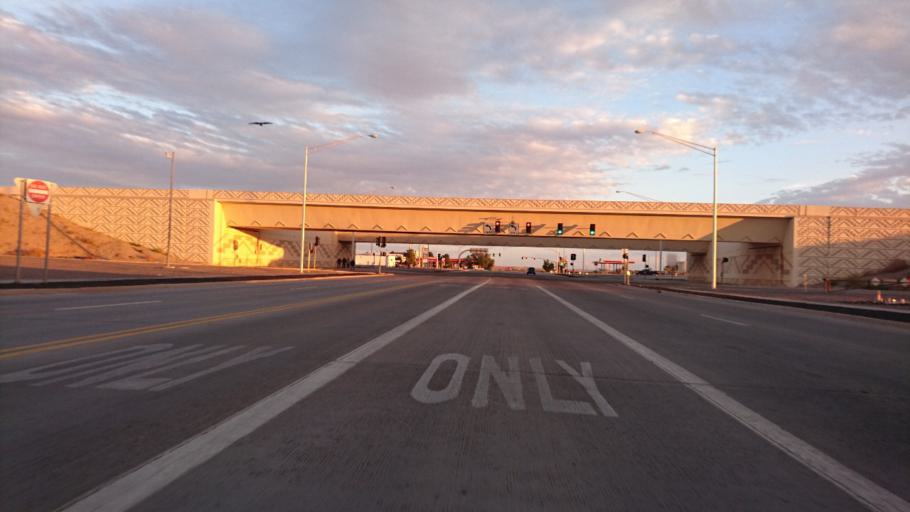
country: US
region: Arizona
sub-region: Navajo County
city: Winslow
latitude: 35.0387
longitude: -110.6979
